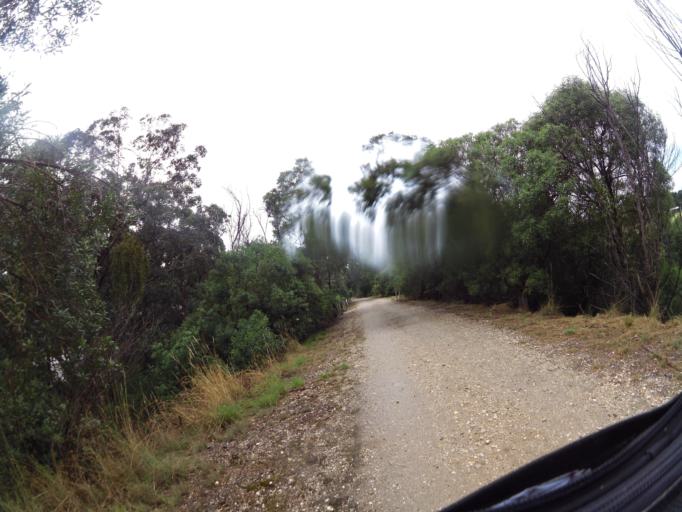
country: AU
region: Victoria
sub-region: East Gippsland
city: Bairnsdale
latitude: -37.8128
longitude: 147.7413
